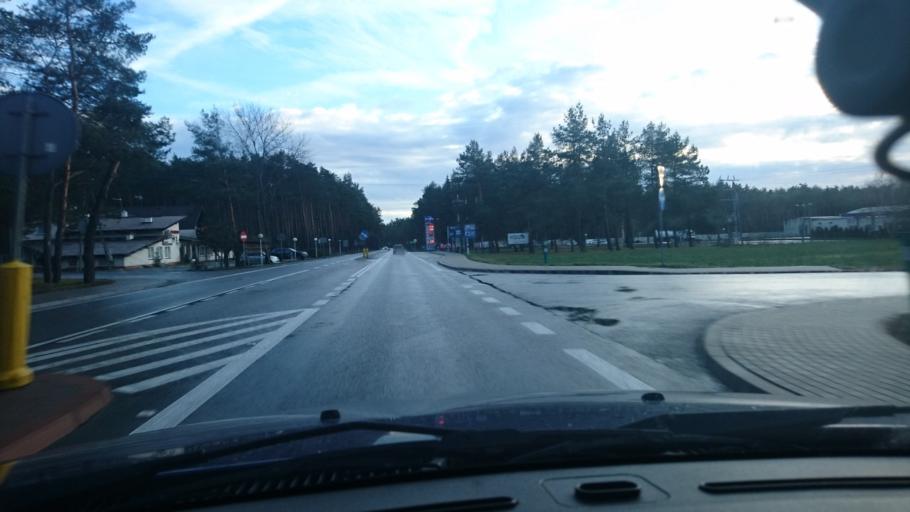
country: PL
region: Greater Poland Voivodeship
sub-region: Powiat kepinski
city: Kepno
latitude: 51.3417
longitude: 17.9522
